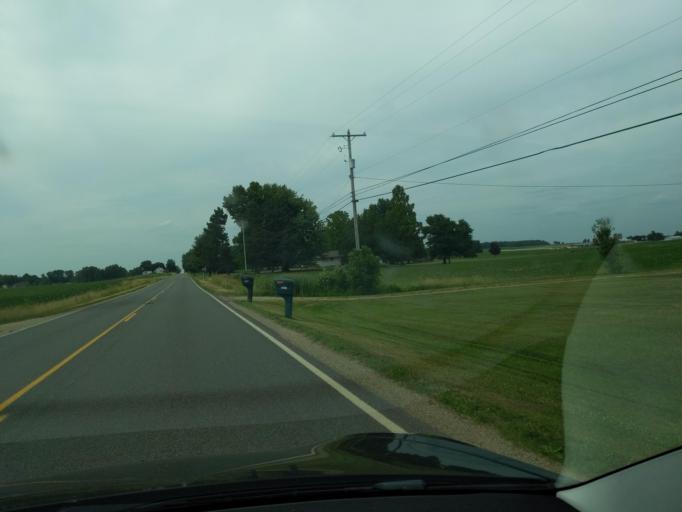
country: US
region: Michigan
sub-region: Clinton County
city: DeWitt
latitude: 42.8461
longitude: -84.6024
